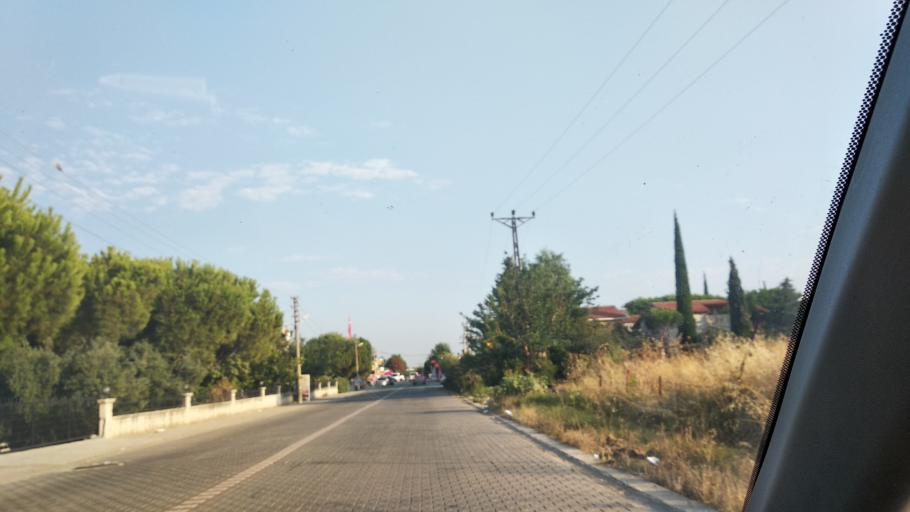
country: TR
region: Balikesir
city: Altinova
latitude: 39.1569
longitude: 26.8239
